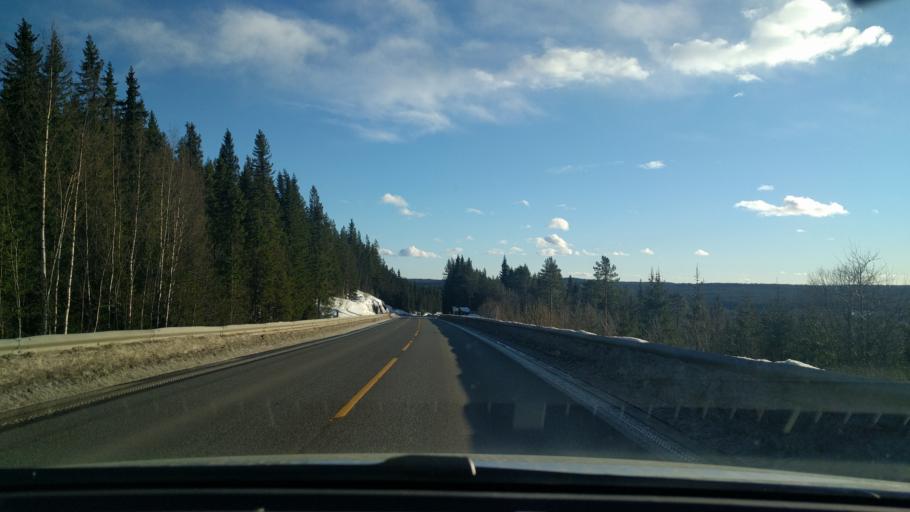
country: NO
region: Hedmark
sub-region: Trysil
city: Innbygda
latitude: 61.0963
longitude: 12.0029
